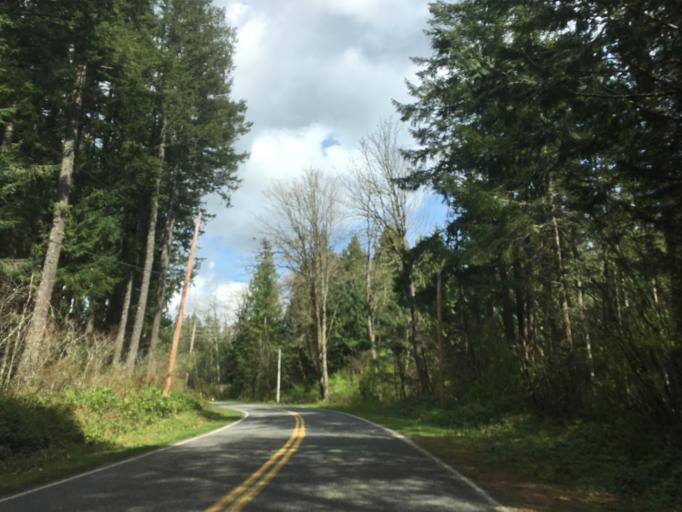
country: US
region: Washington
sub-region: Whatcom County
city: Sudden Valley
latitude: 48.7553
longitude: -122.3516
